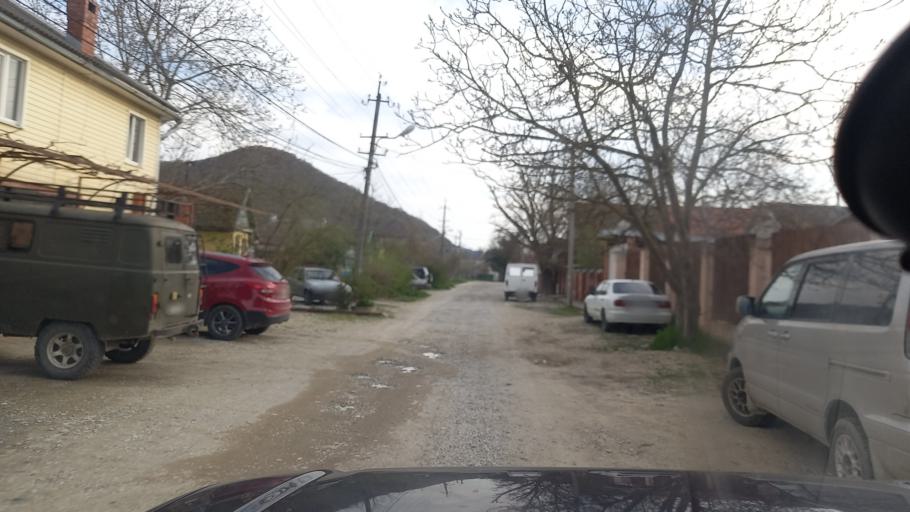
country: RU
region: Krasnodarskiy
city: Arkhipo-Osipovka
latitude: 44.3667
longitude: 38.5431
